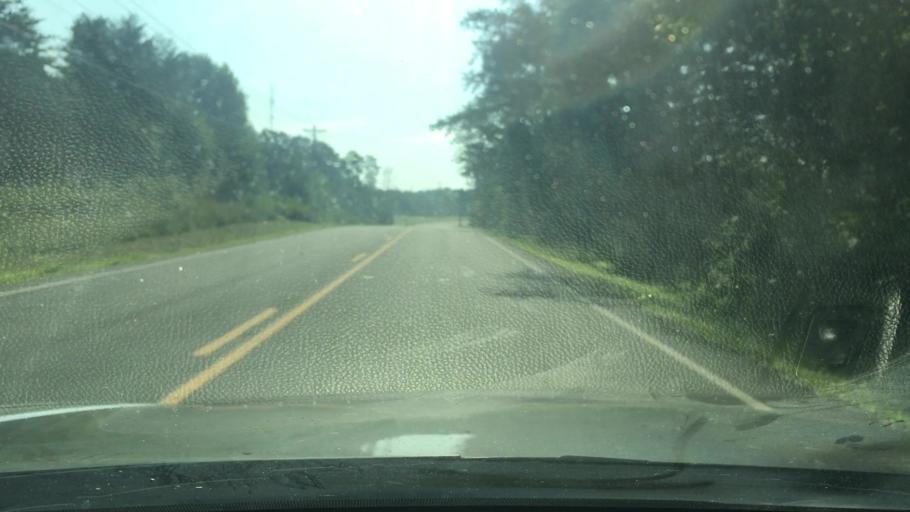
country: US
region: North Carolina
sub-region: Caswell County
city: Yanceyville
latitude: 36.2807
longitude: -79.3534
